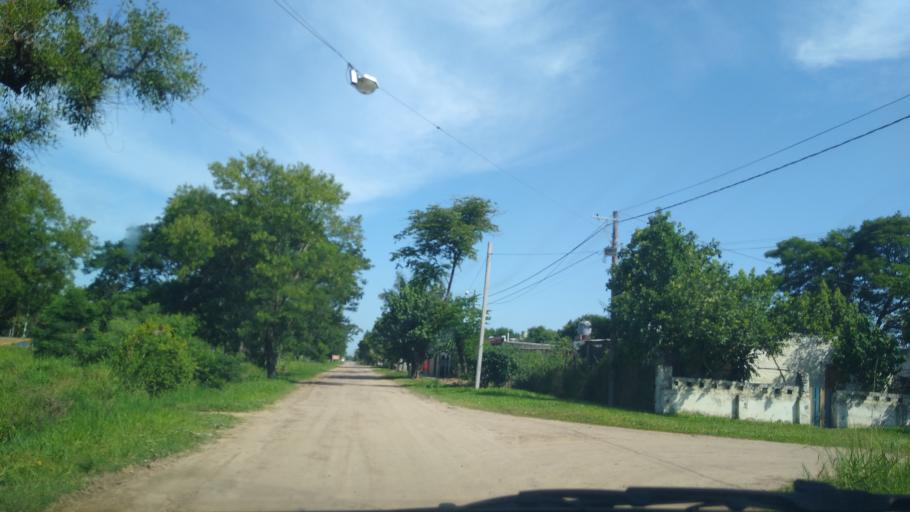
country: AR
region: Chaco
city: Barranqueras
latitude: -27.4879
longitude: -58.9541
